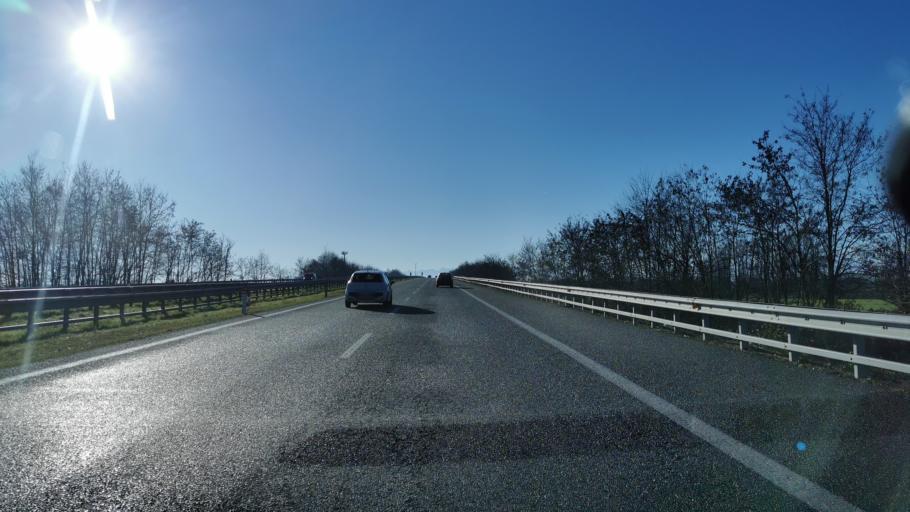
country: IT
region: Piedmont
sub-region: Provincia di Cuneo
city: Caramagna Piemonte
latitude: 44.8128
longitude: 7.7514
